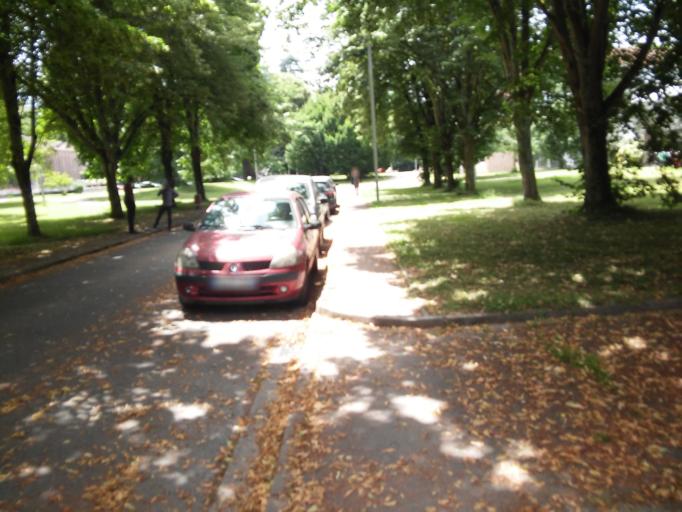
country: FR
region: Aquitaine
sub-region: Departement des Pyrenees-Atlantiques
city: Pau
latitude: 43.3145
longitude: -0.3645
